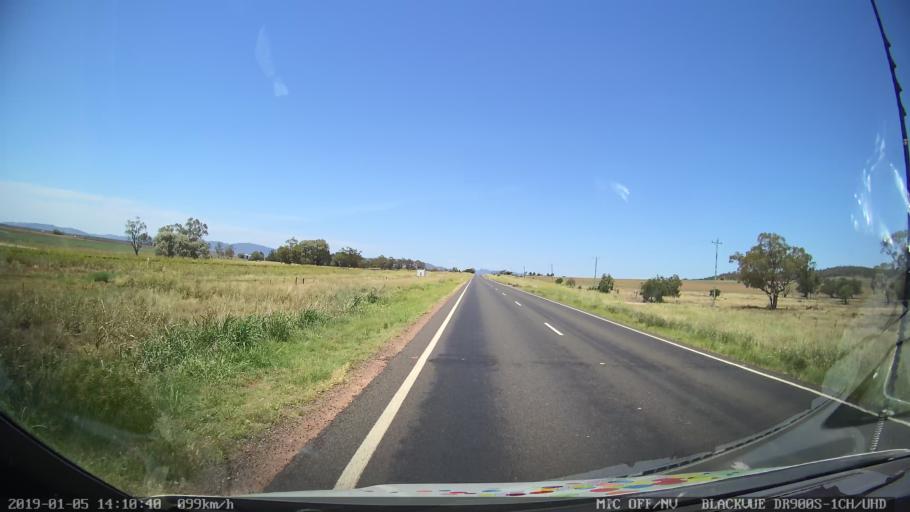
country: AU
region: New South Wales
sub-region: Gunnedah
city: Gunnedah
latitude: -31.2453
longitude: 150.4462
